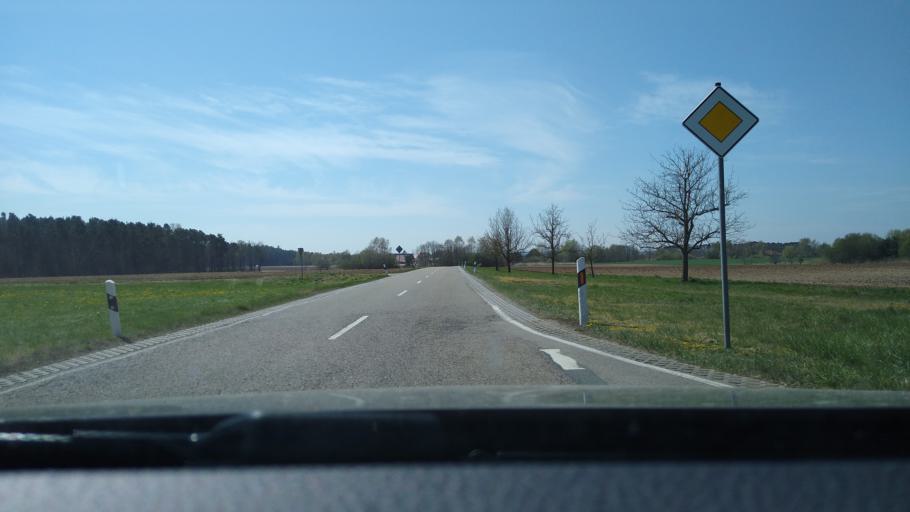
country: DE
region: Bavaria
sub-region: Regierungsbezirk Mittelfranken
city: Merkendorf
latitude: 49.1928
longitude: 10.7249
